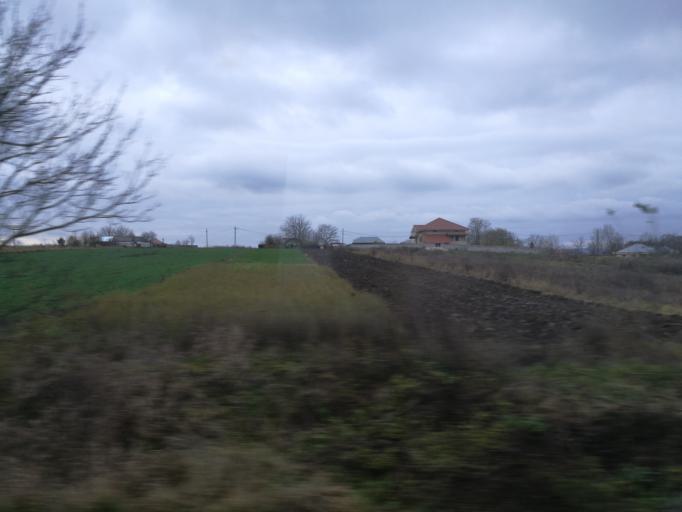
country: RO
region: Bacau
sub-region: Comuna Filipesti
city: Filipesti
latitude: 46.7335
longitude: 26.8843
